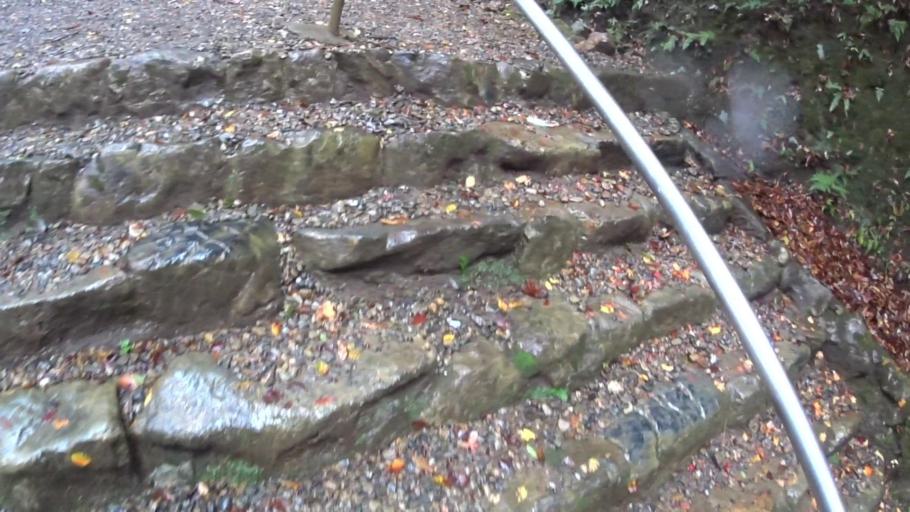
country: JP
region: Kyoto
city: Miyazu
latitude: 35.4287
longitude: 135.1550
